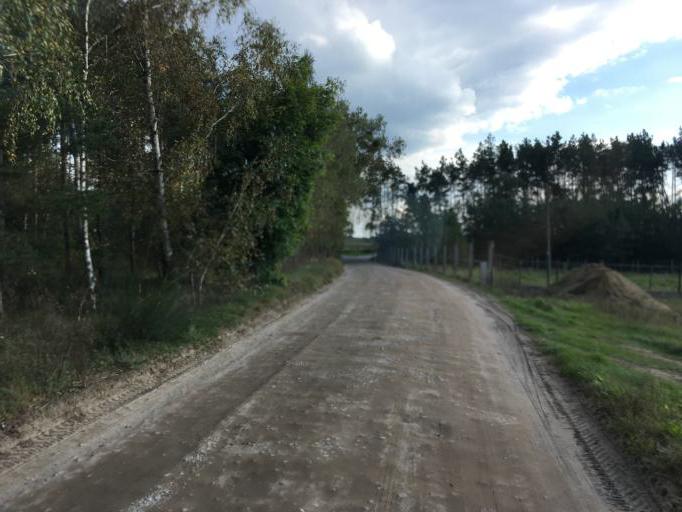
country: PL
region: Kujawsko-Pomorskie
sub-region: Powiat tucholski
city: Tuchola
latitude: 53.6023
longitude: 17.9110
